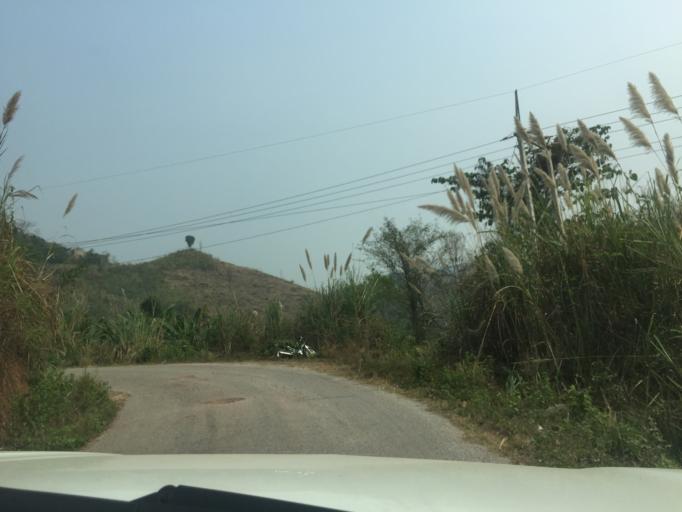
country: LA
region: Xiagnabouli
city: Sainyabuli
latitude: 19.3007
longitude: 101.4825
